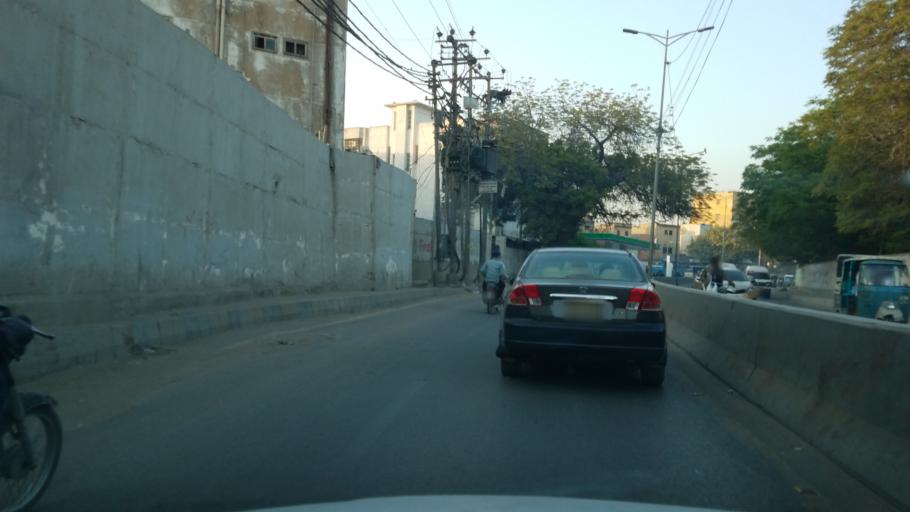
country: PK
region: Sindh
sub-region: Karachi District
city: Karachi
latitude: 24.8717
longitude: 67.0220
